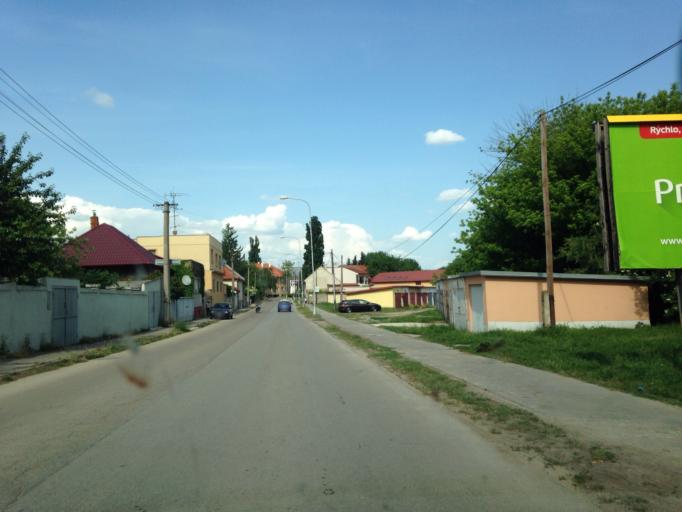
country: SK
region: Nitriansky
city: Komarno
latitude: 47.7592
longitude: 18.1353
